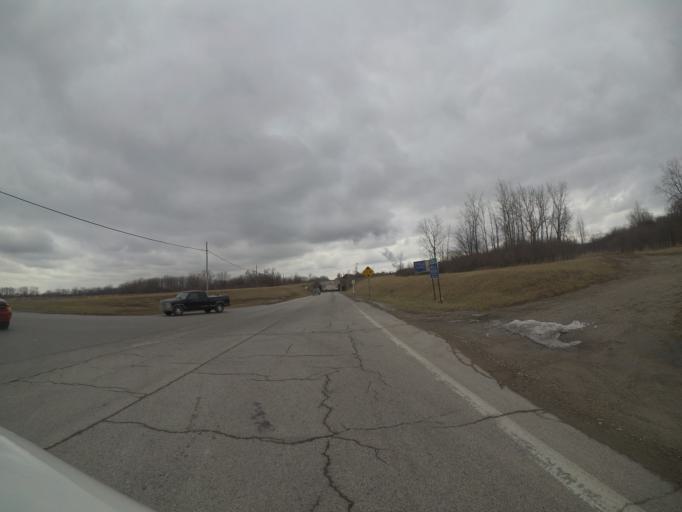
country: US
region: Ohio
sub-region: Wood County
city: Walbridge
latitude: 41.6031
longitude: -83.5122
